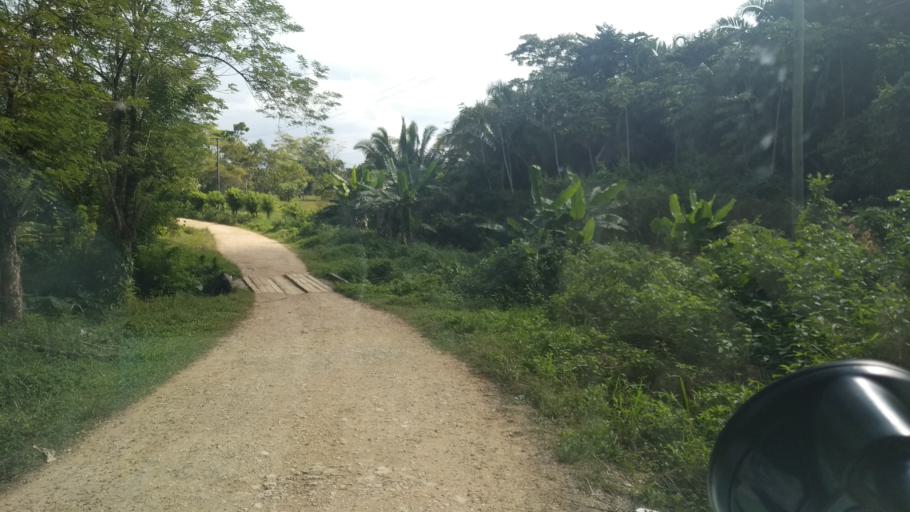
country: BZ
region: Toledo
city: Punta Gorda
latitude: 16.2073
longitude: -88.9148
